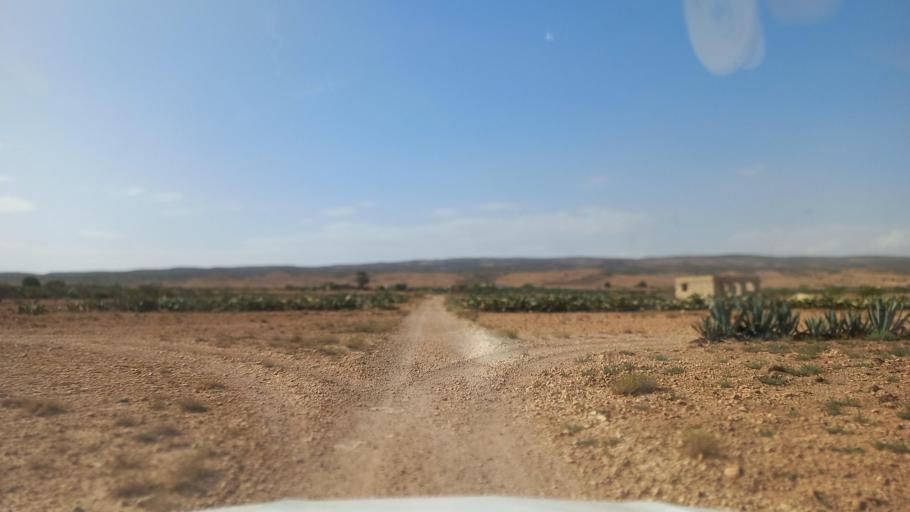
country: TN
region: Al Qasrayn
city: Kasserine
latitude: 35.2849
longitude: 8.9407
